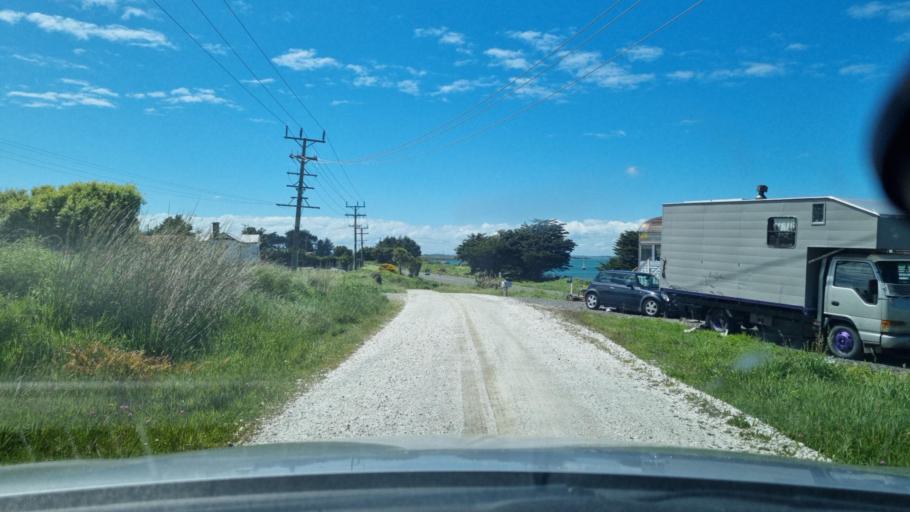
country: NZ
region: Southland
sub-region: Invercargill City
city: Bluff
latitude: -46.5850
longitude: 168.3041
